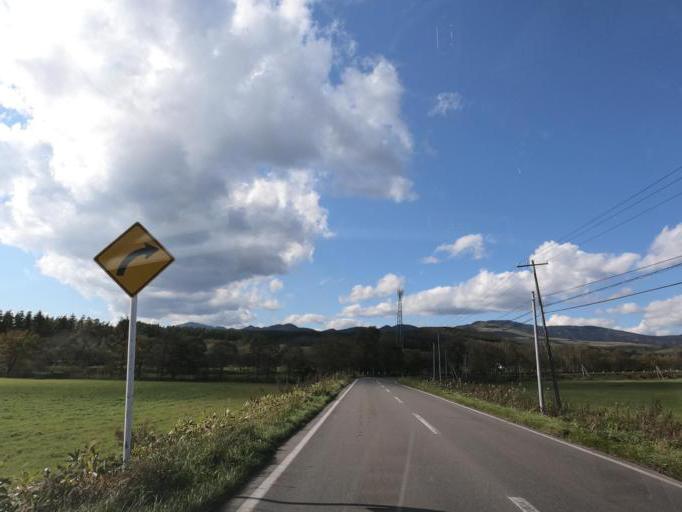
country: JP
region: Hokkaido
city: Otofuke
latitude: 43.2593
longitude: 143.2437
